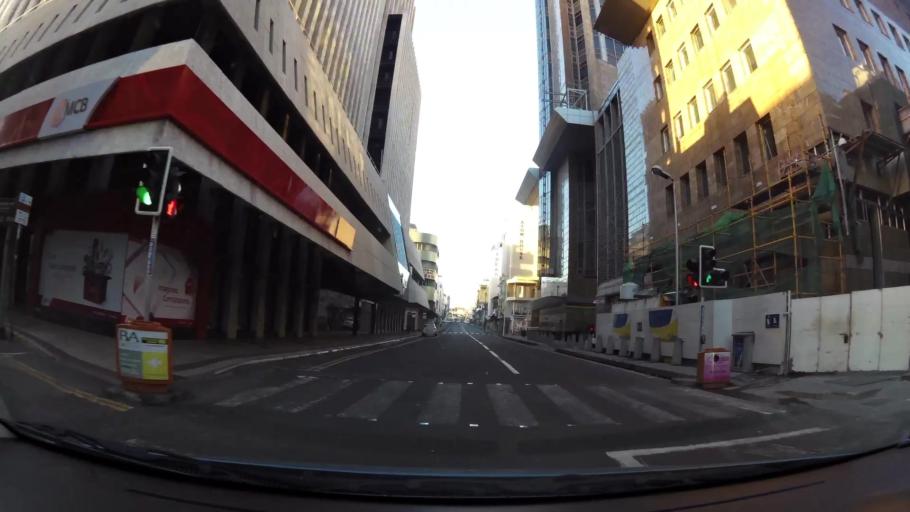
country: MU
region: Port Louis
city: Port Louis
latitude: -20.1619
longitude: 57.5032
